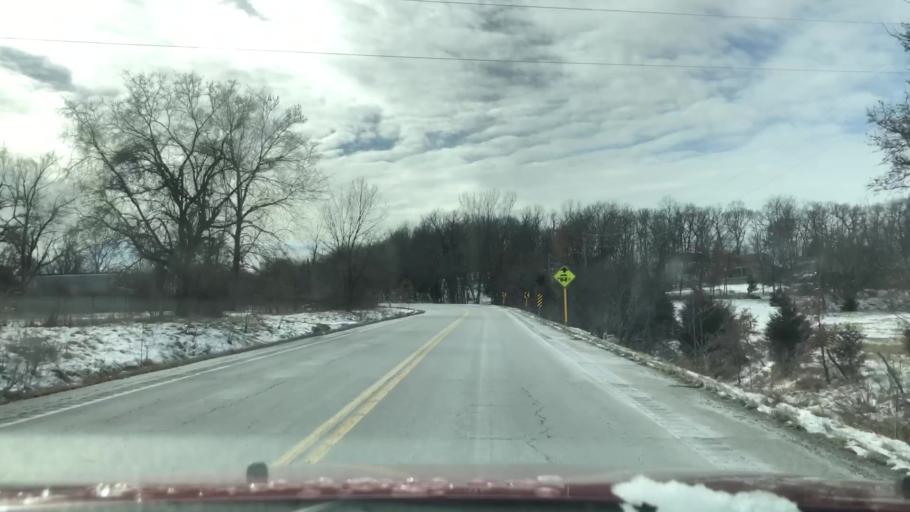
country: US
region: Missouri
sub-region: Jackson County
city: Lone Jack
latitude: 38.8973
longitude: -94.1346
